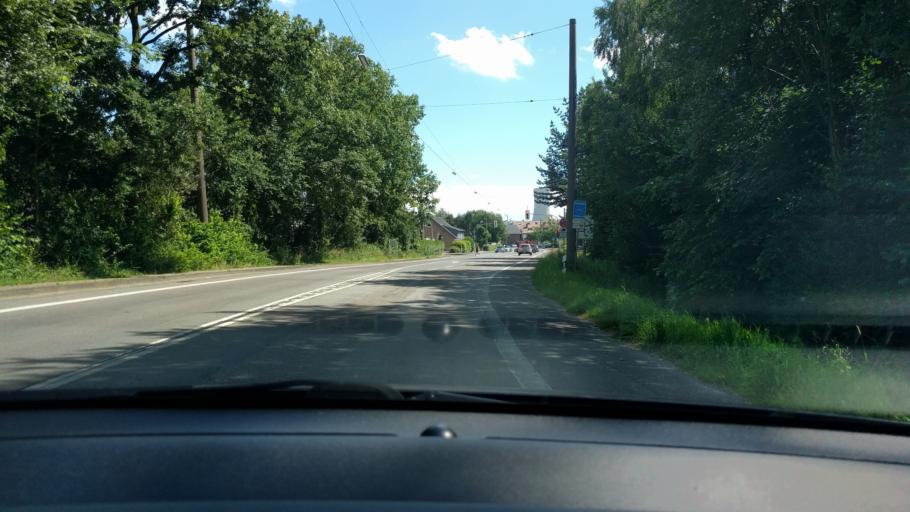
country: DE
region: North Rhine-Westphalia
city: Datteln
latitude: 51.6583
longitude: 7.3368
